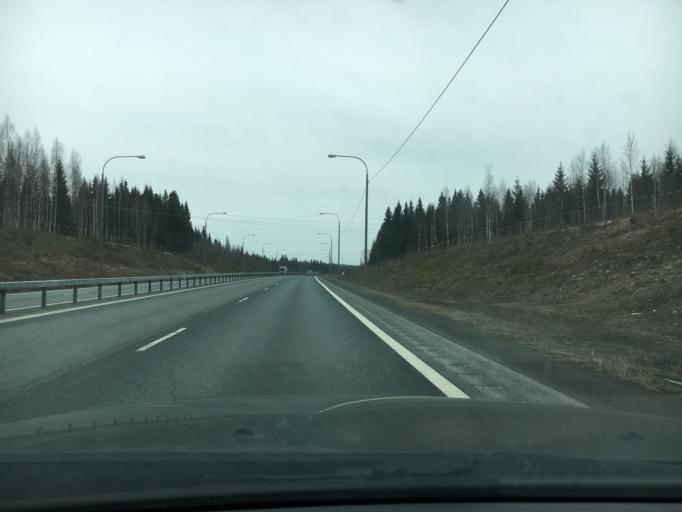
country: FI
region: Northern Savo
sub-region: Kuopio
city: Kuopio
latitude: 62.7620
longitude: 27.5809
